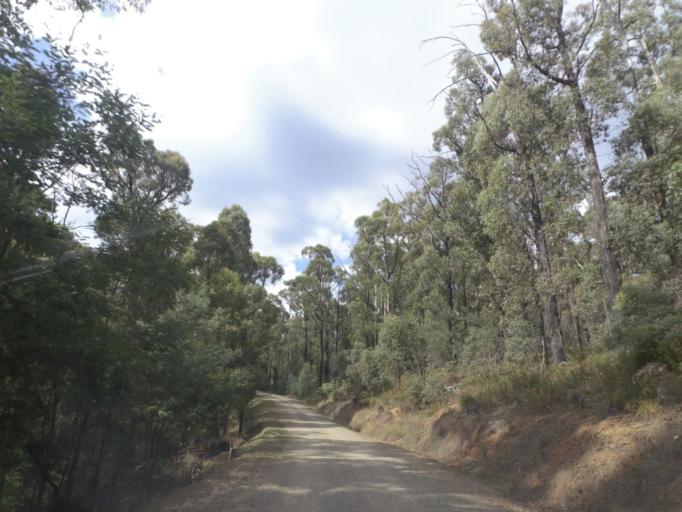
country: AU
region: Victoria
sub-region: Yarra Ranges
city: Healesville
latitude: -37.5348
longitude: 145.7079
